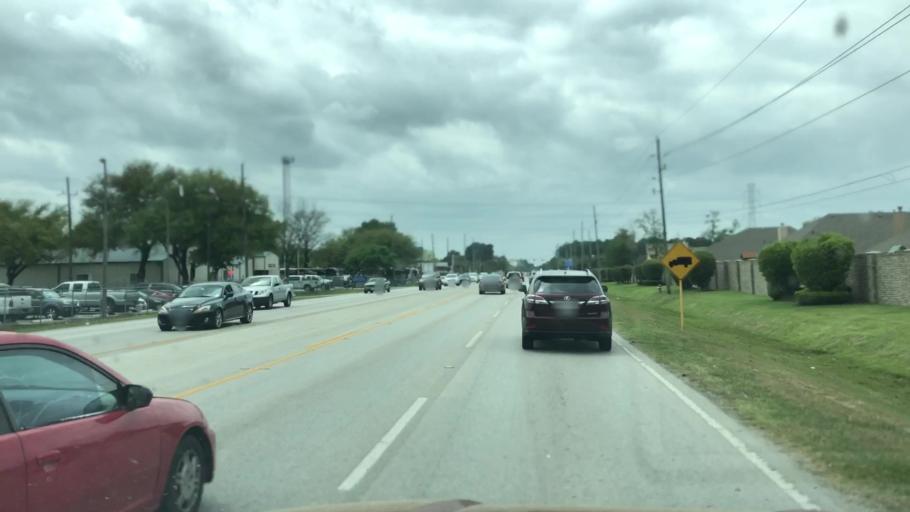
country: US
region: Texas
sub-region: Harris County
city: Spring
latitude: 30.0522
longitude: -95.4901
